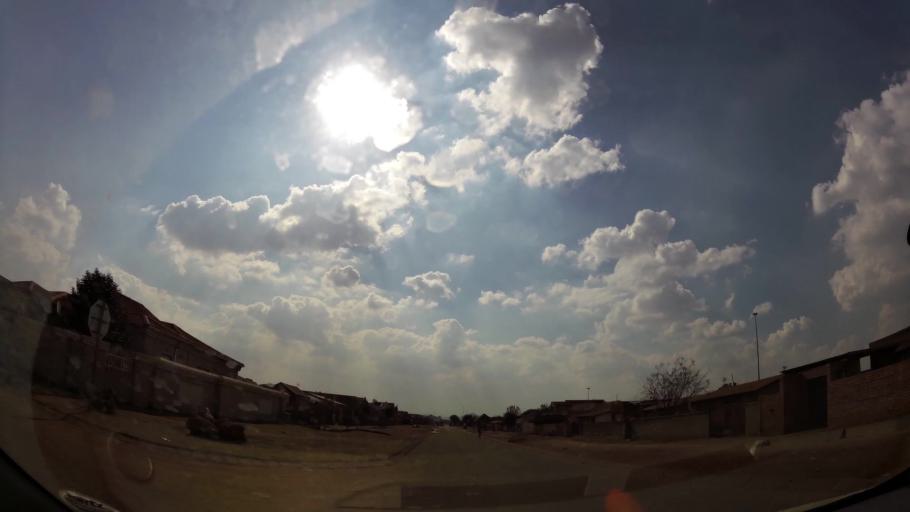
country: ZA
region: Gauteng
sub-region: Ekurhuleni Metropolitan Municipality
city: Germiston
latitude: -26.3513
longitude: 28.1652
